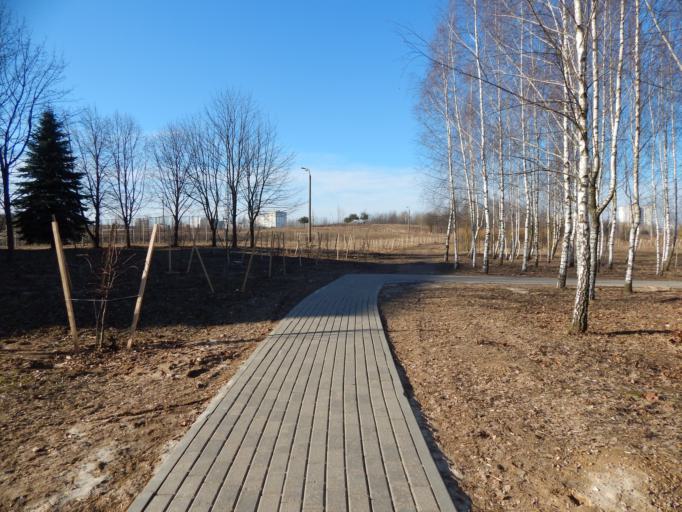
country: BY
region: Minsk
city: Novoye Medvezhino
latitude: 53.9103
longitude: 27.4678
